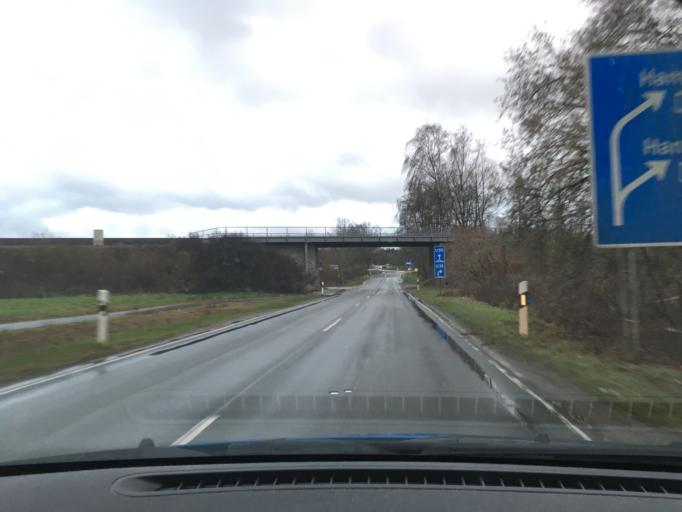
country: DE
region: Lower Saxony
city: Bad Fallingbostel
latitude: 52.8943
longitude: 9.7648
